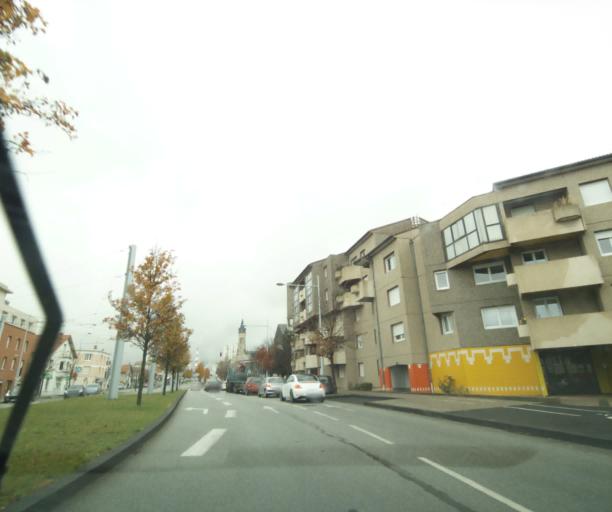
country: FR
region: Auvergne
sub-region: Departement du Puy-de-Dome
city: Aubiere
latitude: 45.7636
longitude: 3.1001
